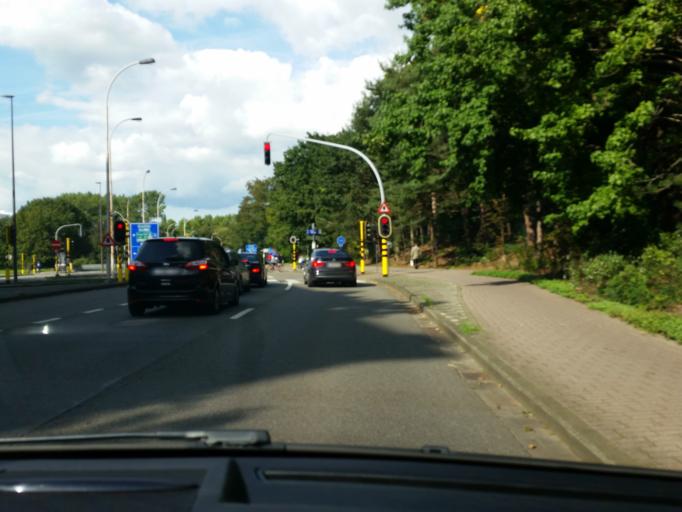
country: BE
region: Flanders
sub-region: Provincie Antwerpen
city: Antwerpen
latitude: 51.1861
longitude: 4.4052
